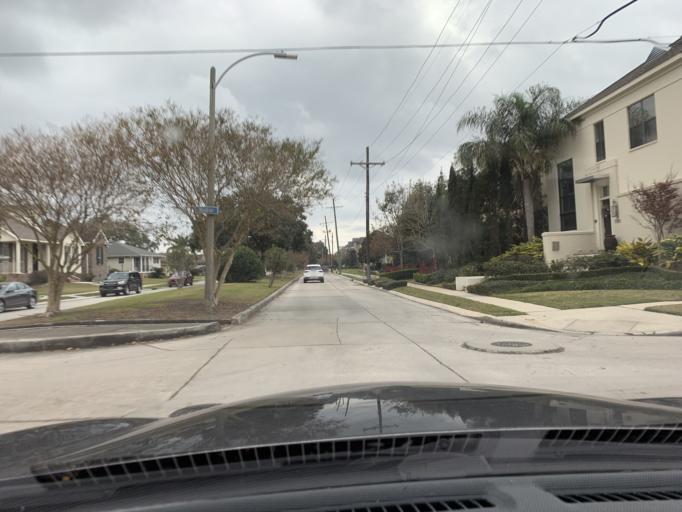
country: US
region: Louisiana
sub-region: Jefferson Parish
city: Metairie
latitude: 30.0173
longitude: -90.1013
